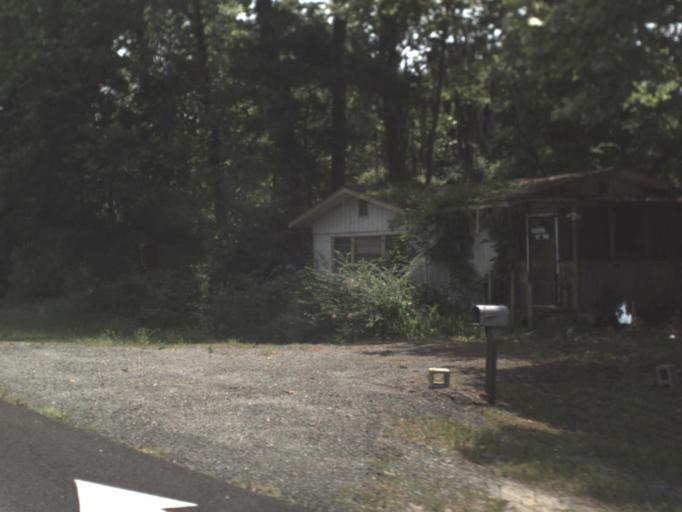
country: US
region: Florida
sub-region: Nassau County
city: Yulee
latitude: 30.6286
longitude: -81.6150
